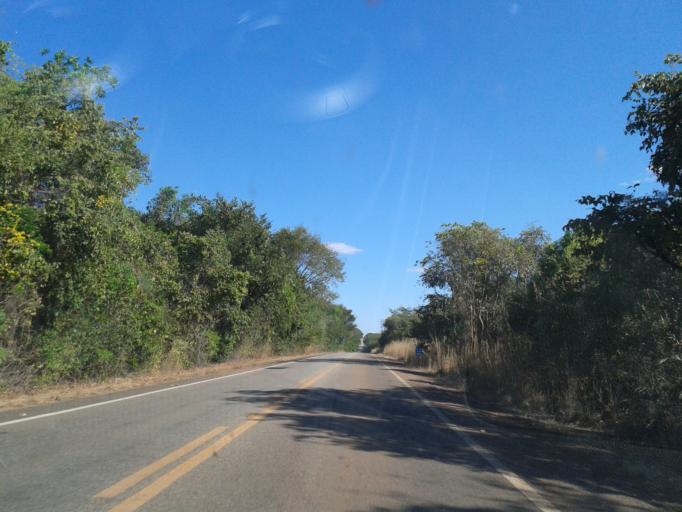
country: BR
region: Goias
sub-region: Mozarlandia
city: Mozarlandia
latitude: -14.4257
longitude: -50.4526
